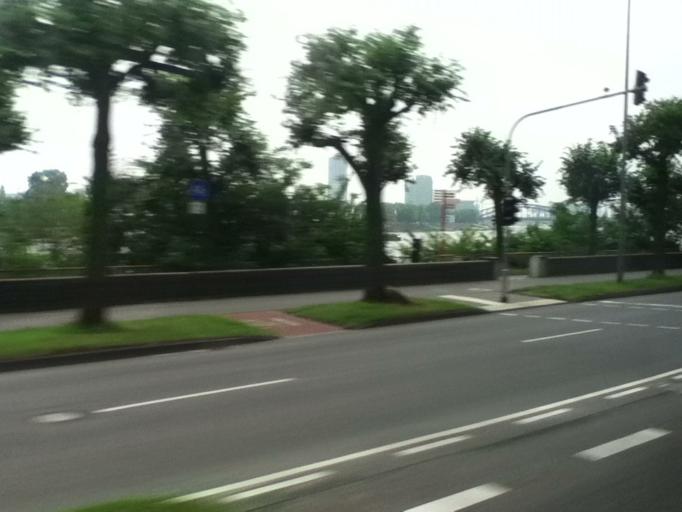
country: DE
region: North Rhine-Westphalia
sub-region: Regierungsbezirk Koln
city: Riehl
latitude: 50.9520
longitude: 6.9682
